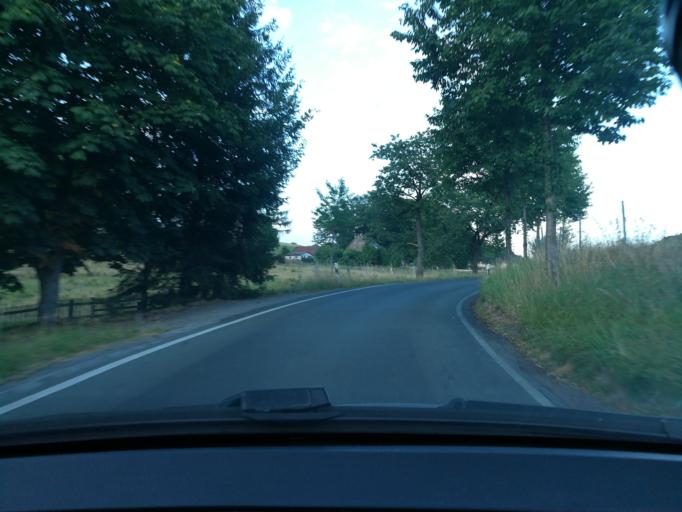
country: DE
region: Lower Saxony
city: Hagen
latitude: 52.1739
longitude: 7.9522
